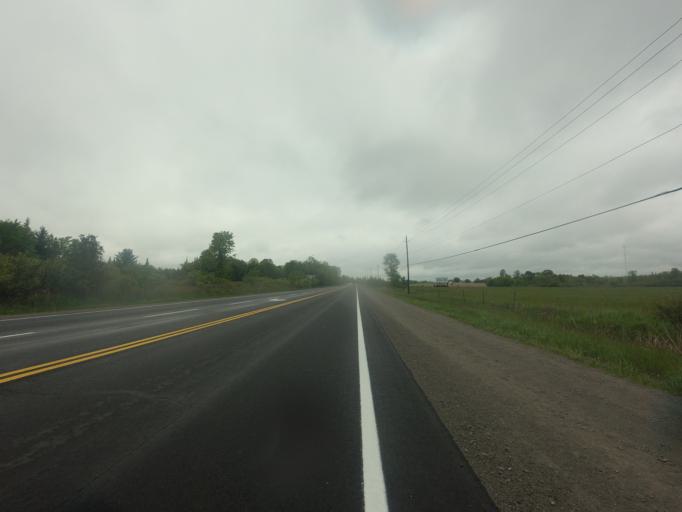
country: CA
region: Ontario
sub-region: Lanark County
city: Smiths Falls
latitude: 44.7499
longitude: -76.1303
